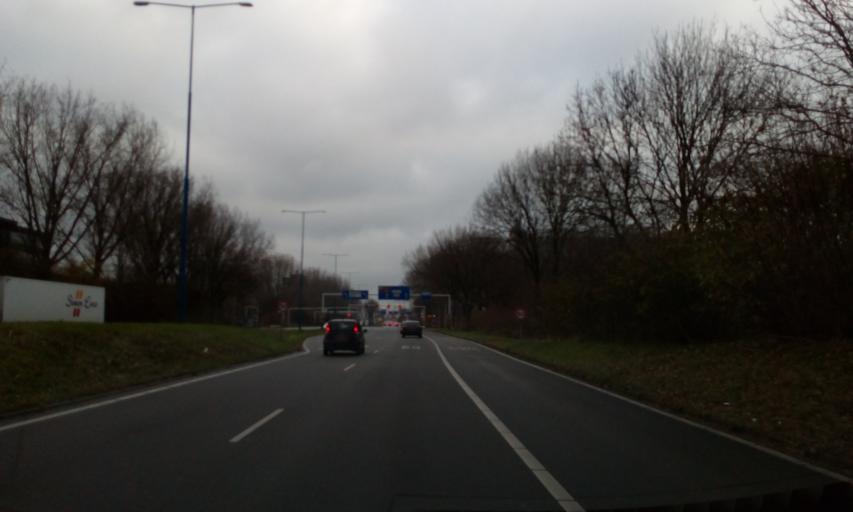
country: NL
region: South Holland
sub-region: Gemeente Zoetermeer
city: Zoetermeer
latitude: 52.0537
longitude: 4.4784
